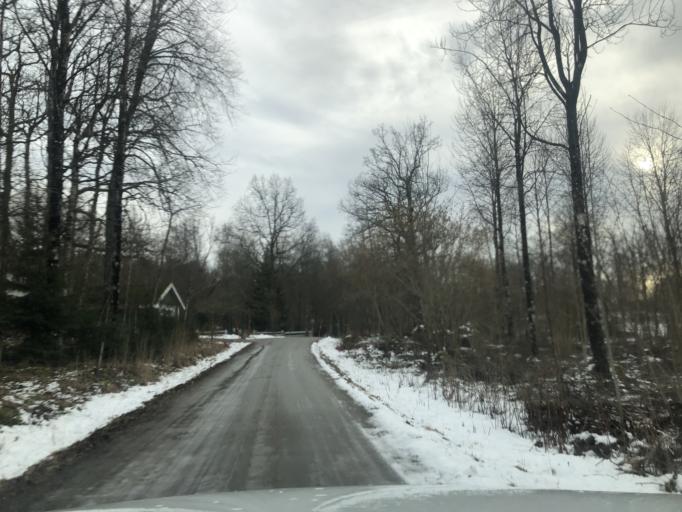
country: SE
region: Vaestra Goetaland
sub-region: Ulricehamns Kommun
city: Ulricehamn
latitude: 57.7700
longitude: 13.4700
